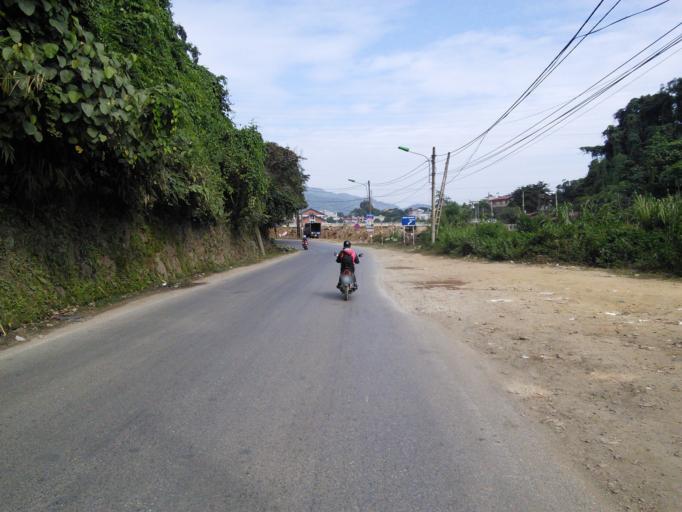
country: VN
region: Lao Cai
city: Lao Cai
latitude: 22.4732
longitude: 103.9716
